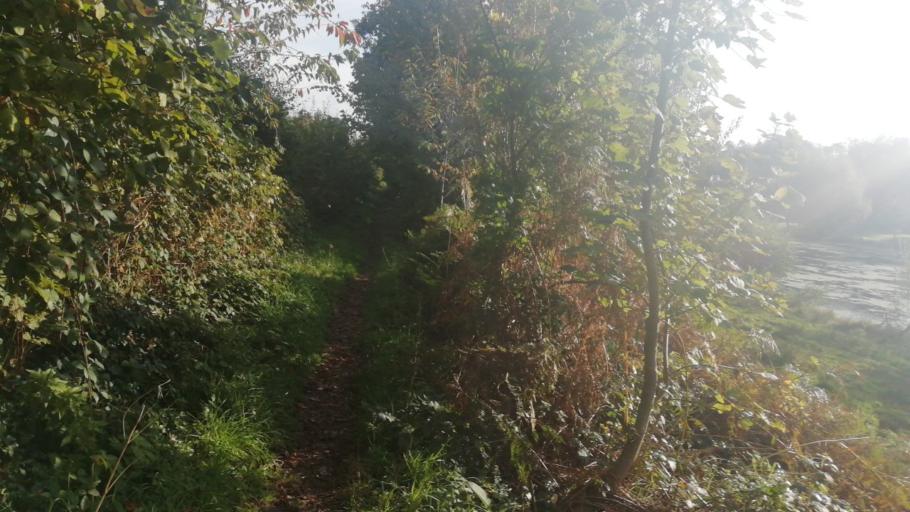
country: FR
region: Haute-Normandie
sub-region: Departement de la Seine-Maritime
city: Rolleville
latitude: 49.5851
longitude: 0.2147
